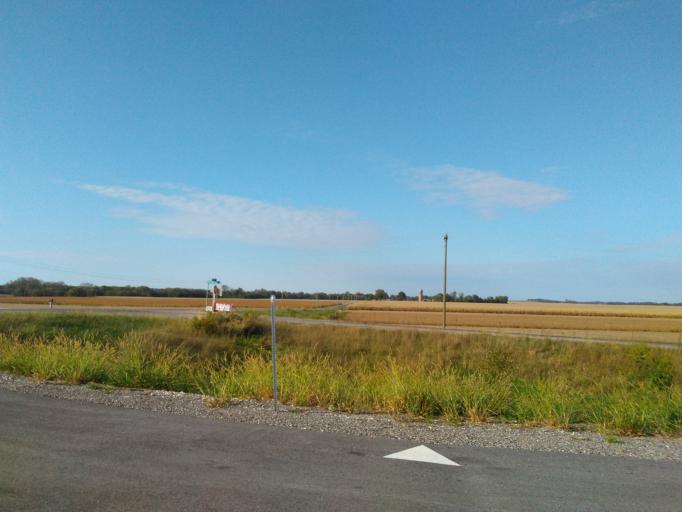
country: US
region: Illinois
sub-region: Madison County
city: Highland
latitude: 38.7877
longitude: -89.6309
